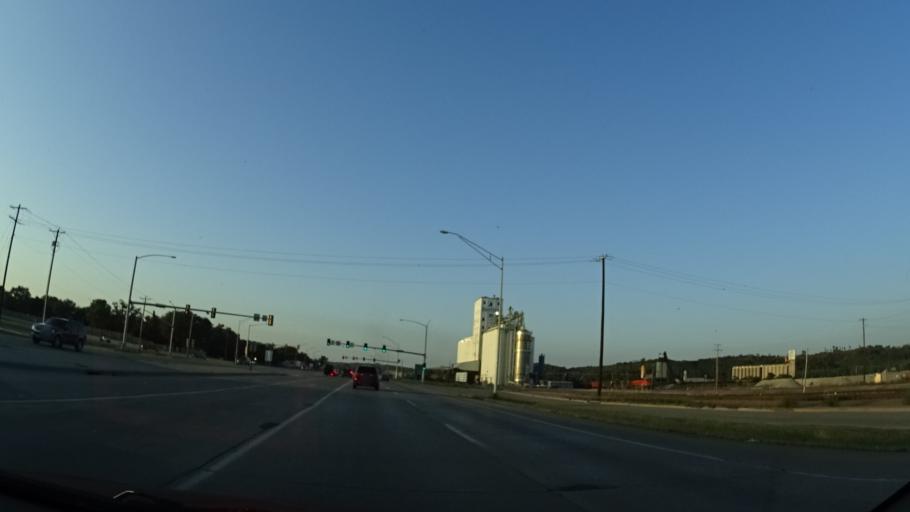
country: US
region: Iowa
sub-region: Pottawattamie County
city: Council Bluffs
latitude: 41.2326
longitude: -95.8513
